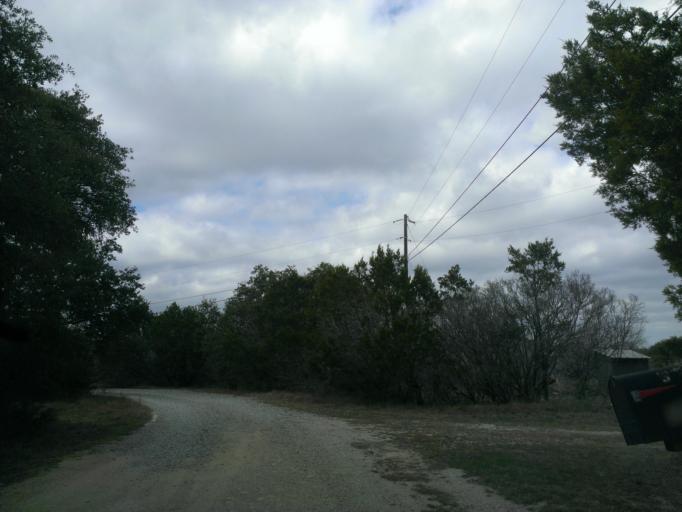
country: US
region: Texas
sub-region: Travis County
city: Briarcliff
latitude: 30.3895
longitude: -98.0906
